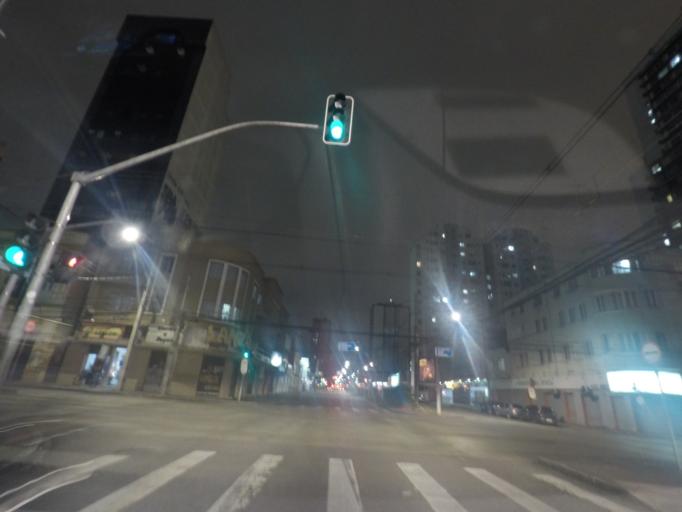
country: BR
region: Parana
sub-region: Curitiba
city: Curitiba
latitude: -25.4366
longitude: -49.2690
